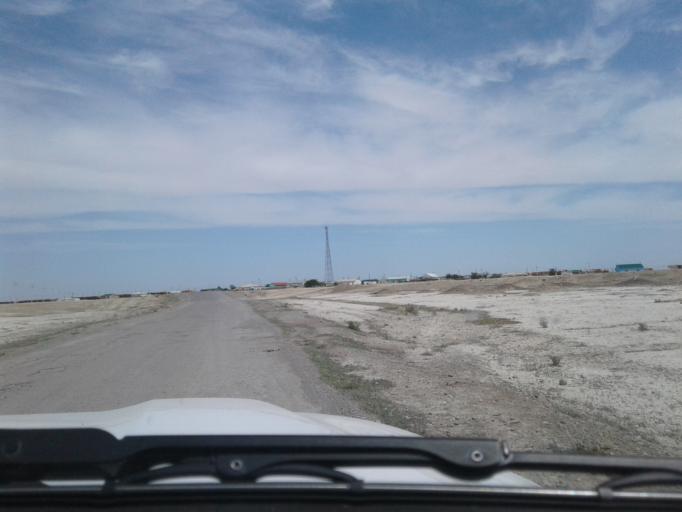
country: TM
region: Balkan
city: Gazanjyk
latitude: 39.2054
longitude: 55.7101
